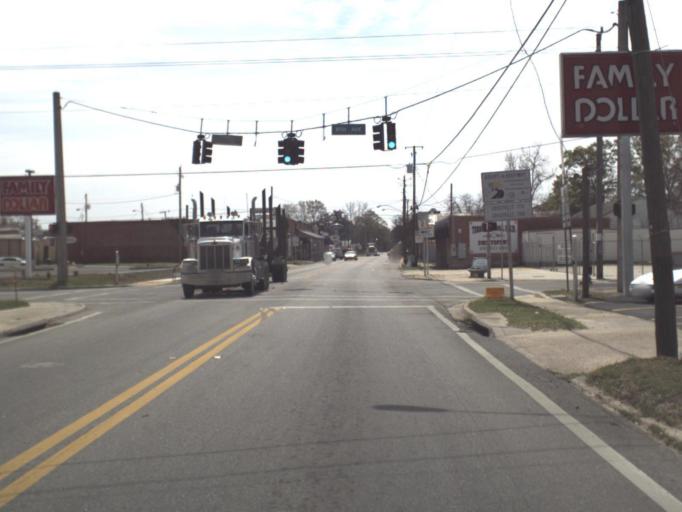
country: US
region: Florida
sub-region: Jackson County
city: Graceville
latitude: 30.9576
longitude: -85.5167
